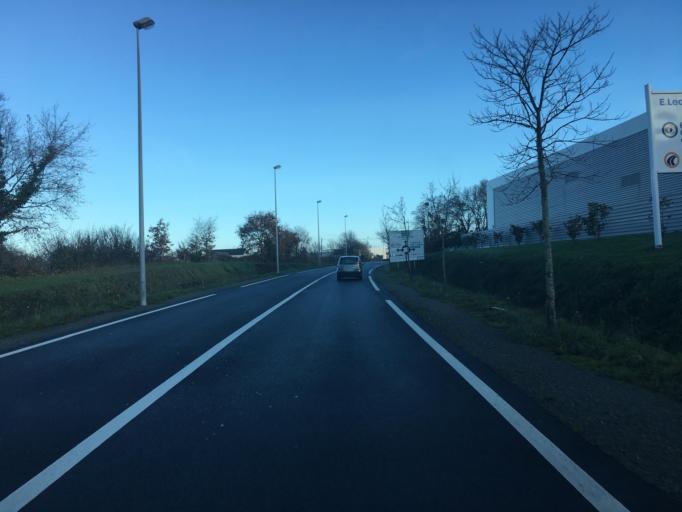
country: FR
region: Pays de la Loire
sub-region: Departement de la Loire-Atlantique
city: Pontchateau
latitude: 47.4337
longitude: -2.0832
